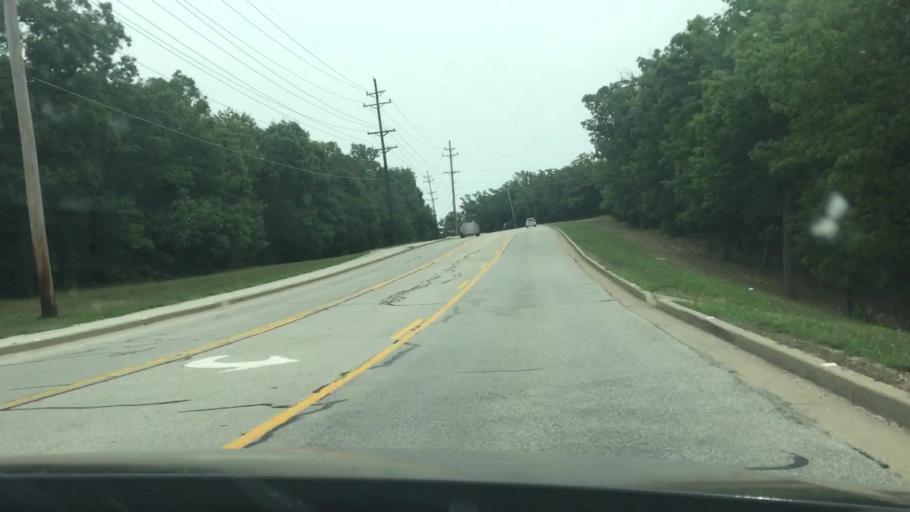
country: US
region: Missouri
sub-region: Camden County
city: Four Seasons
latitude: 38.1924
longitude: -92.7032
